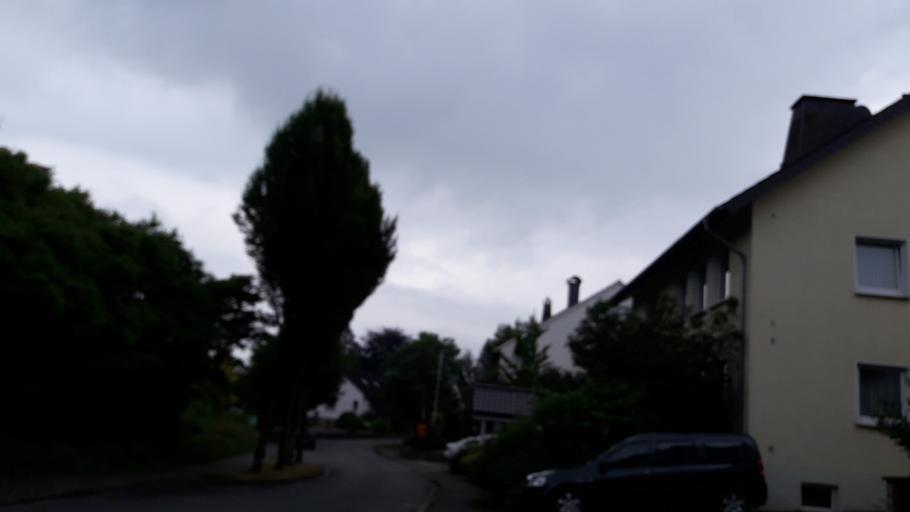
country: DE
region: North Rhine-Westphalia
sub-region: Regierungsbezirk Detmold
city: Salzkotten
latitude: 51.6329
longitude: 8.6748
